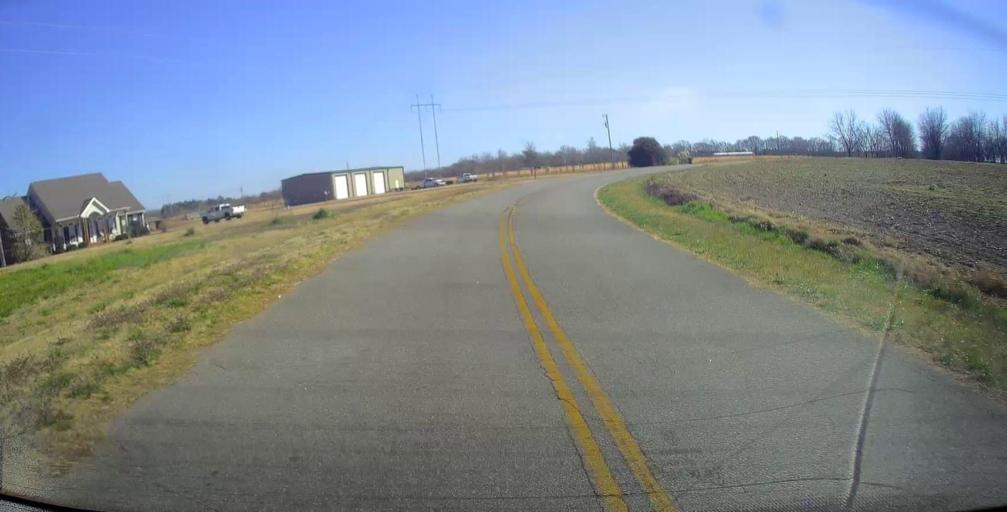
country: US
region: Georgia
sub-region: Peach County
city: Byron
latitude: 32.6289
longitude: -83.8401
